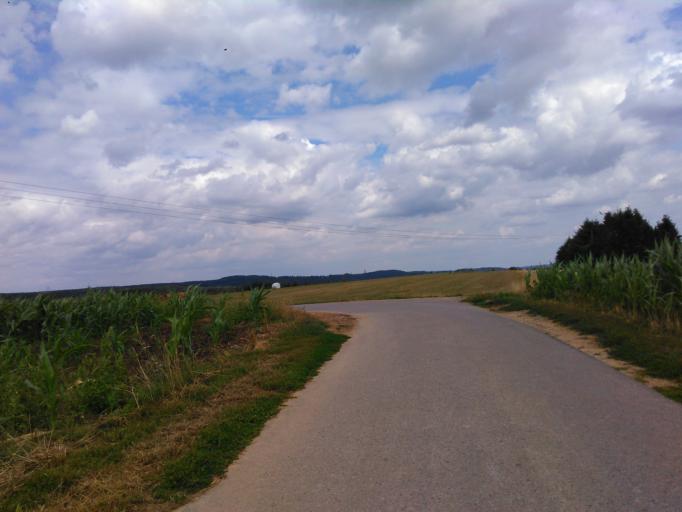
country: LU
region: Grevenmacher
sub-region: Canton de Grevenmacher
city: Junglinster
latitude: 49.7191
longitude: 6.2758
